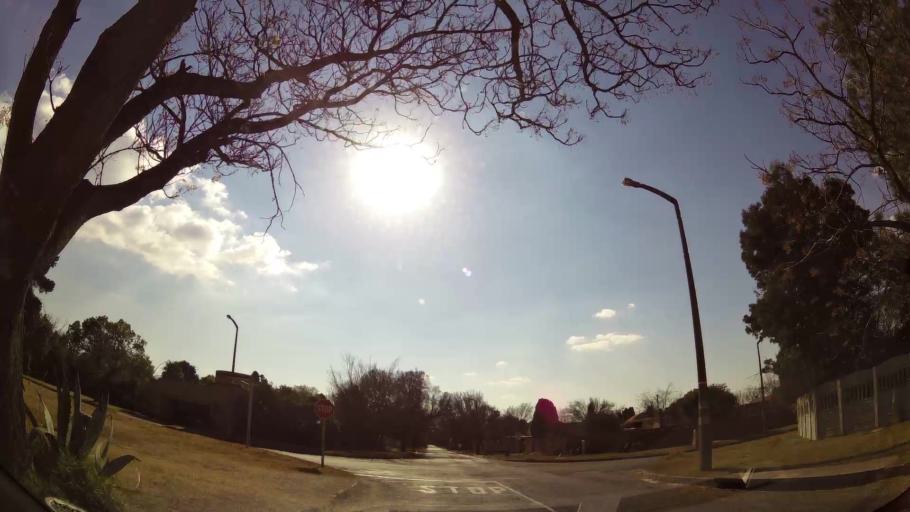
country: ZA
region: Gauteng
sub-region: Ekurhuleni Metropolitan Municipality
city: Benoni
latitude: -26.1453
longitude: 28.3450
